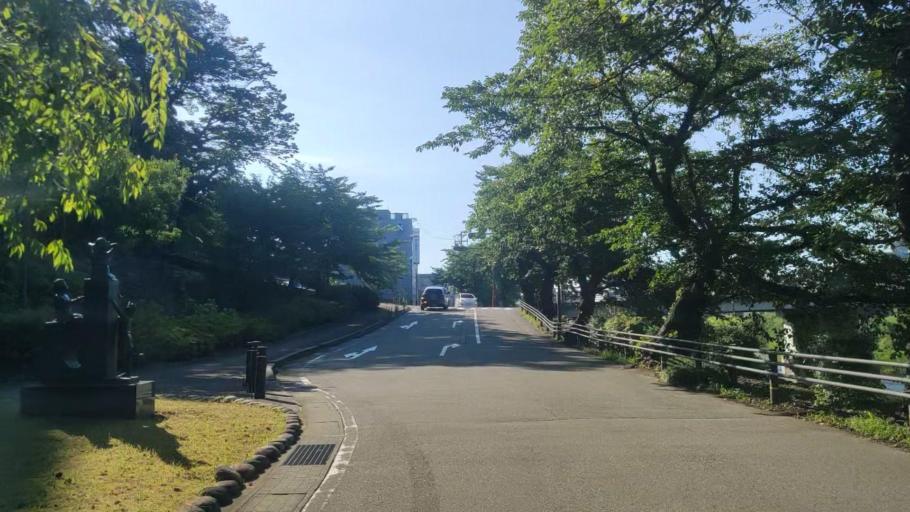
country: JP
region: Ishikawa
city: Nonoichi
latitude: 36.5528
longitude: 136.6555
